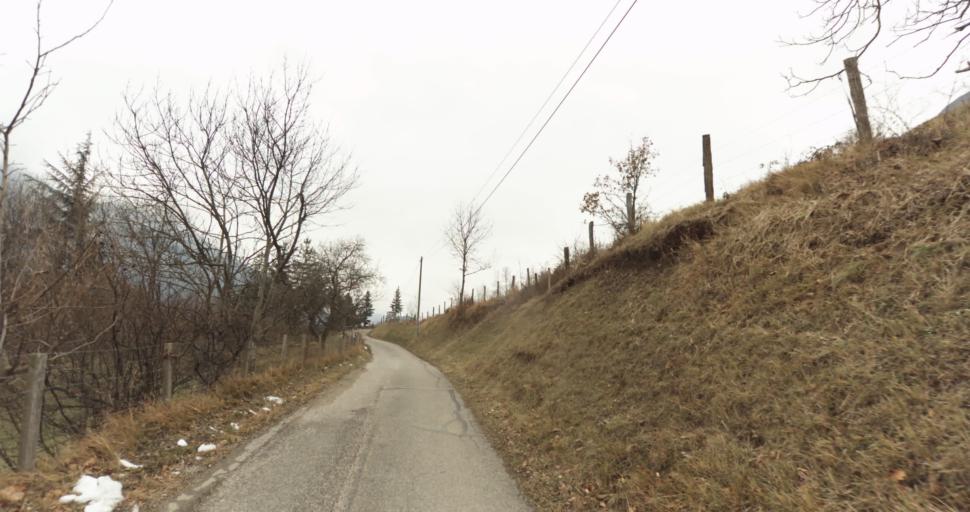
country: FR
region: Rhone-Alpes
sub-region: Departement de l'Isere
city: Saint-Georges-de-Commiers
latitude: 45.0248
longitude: 5.6890
